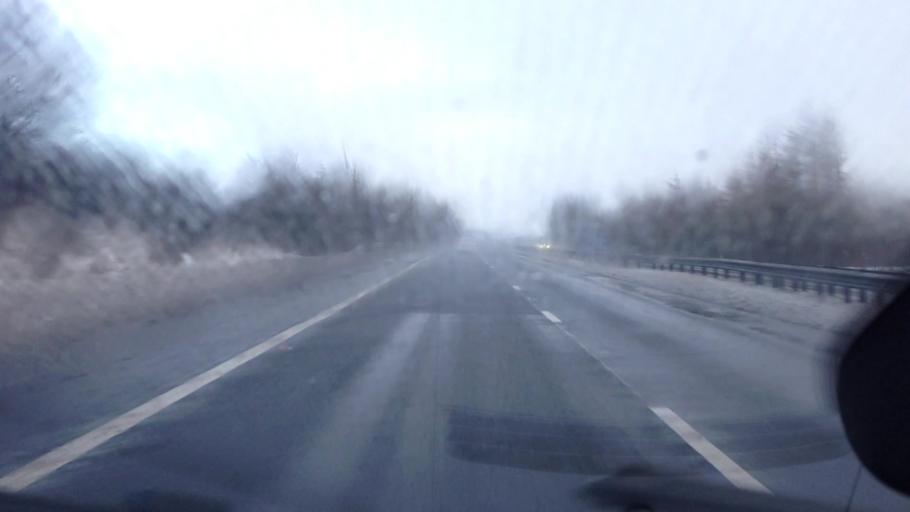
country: GB
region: Scotland
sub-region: South Lanarkshire
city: Blackwood
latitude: 55.6596
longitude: -3.9149
